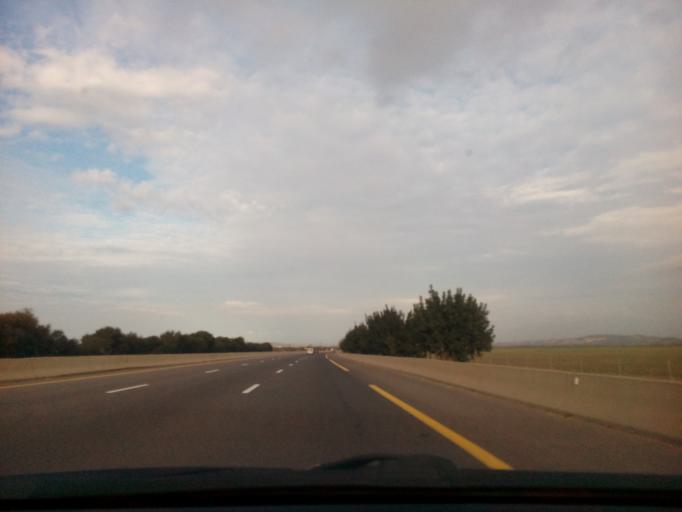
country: DZ
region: Mostaganem
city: Mostaganem
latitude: 35.6813
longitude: 0.1547
